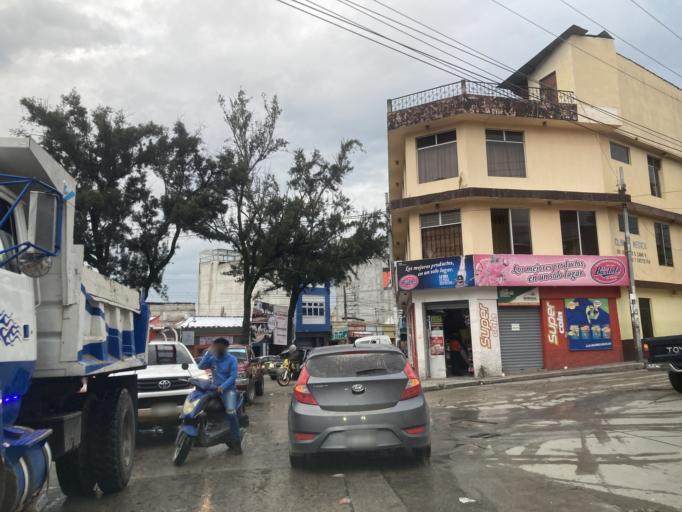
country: GT
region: Huehuetenango
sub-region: Municipio de Huehuetenango
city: Huehuetenango
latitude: 15.3239
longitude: -91.4681
